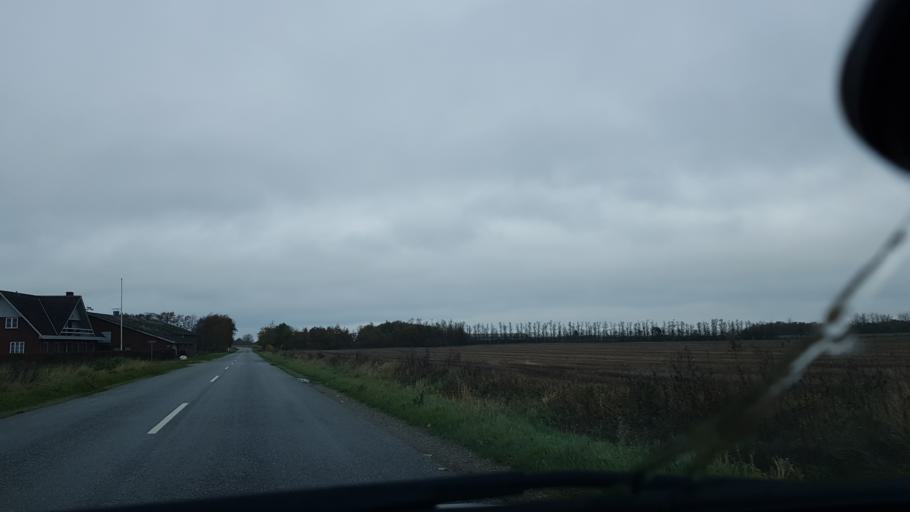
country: DK
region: South Denmark
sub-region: Tonder Kommune
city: Sherrebek
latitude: 55.2335
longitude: 8.8350
